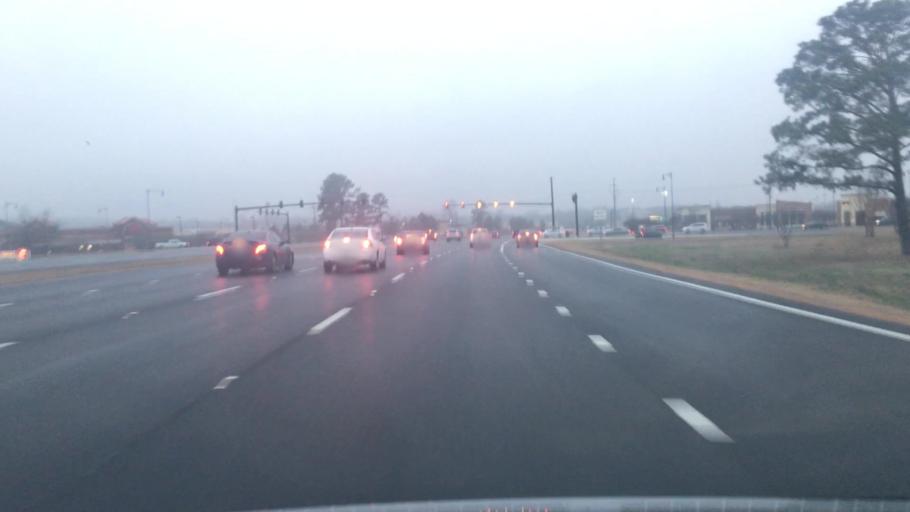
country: US
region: Mississippi
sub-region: Rankin County
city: Flowood
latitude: 32.3408
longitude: -90.0627
